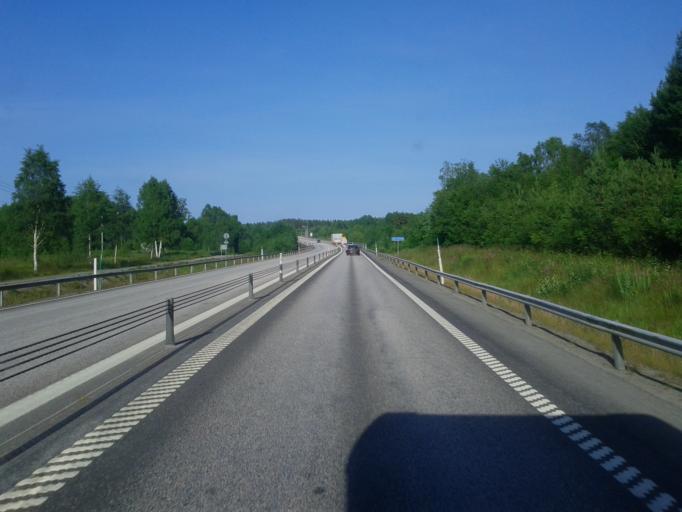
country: SE
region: Vaesterbotten
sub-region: Umea Kommun
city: Saevar
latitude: 63.8967
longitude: 20.5503
